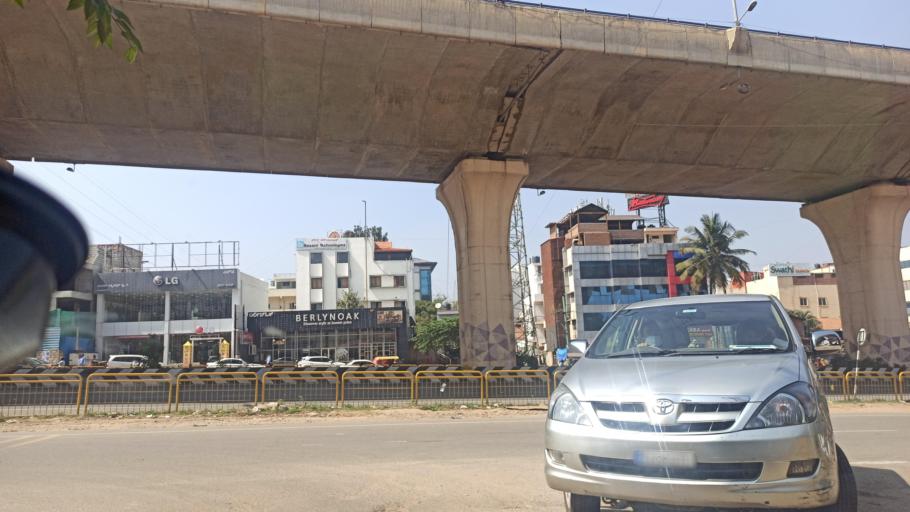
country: IN
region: Karnataka
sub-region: Bangalore Urban
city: Yelahanka
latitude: 13.0584
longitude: 77.5940
